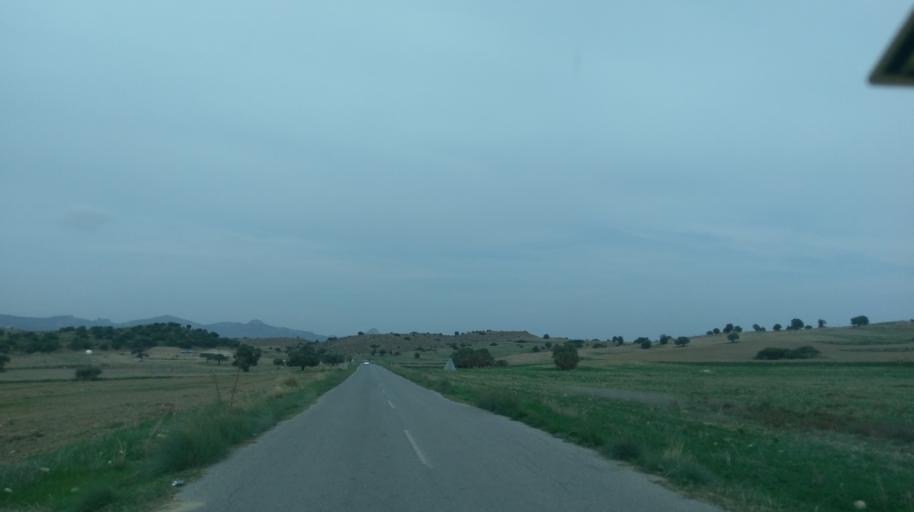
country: CY
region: Ammochostos
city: Trikomo
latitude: 35.3375
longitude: 33.9296
